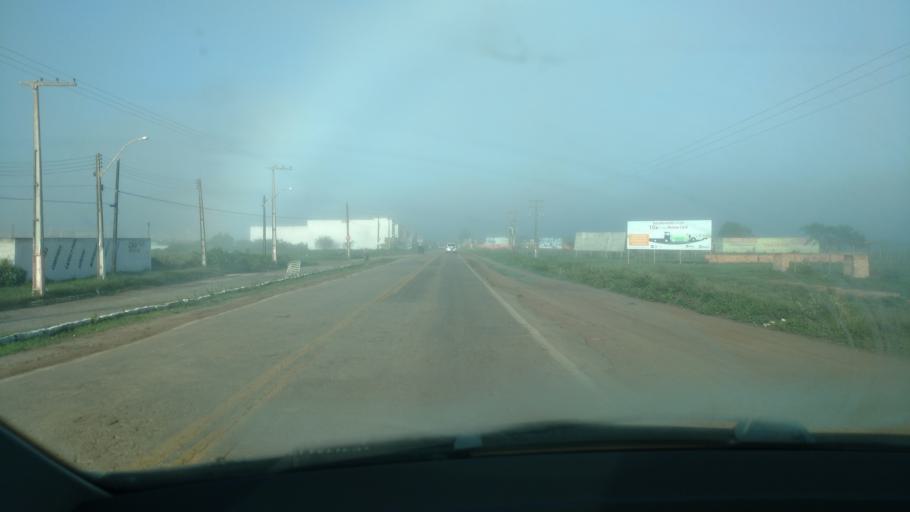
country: BR
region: Sergipe
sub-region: Tobias Barreto
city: Tobias Barreto
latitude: -11.1714
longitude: -37.9866
